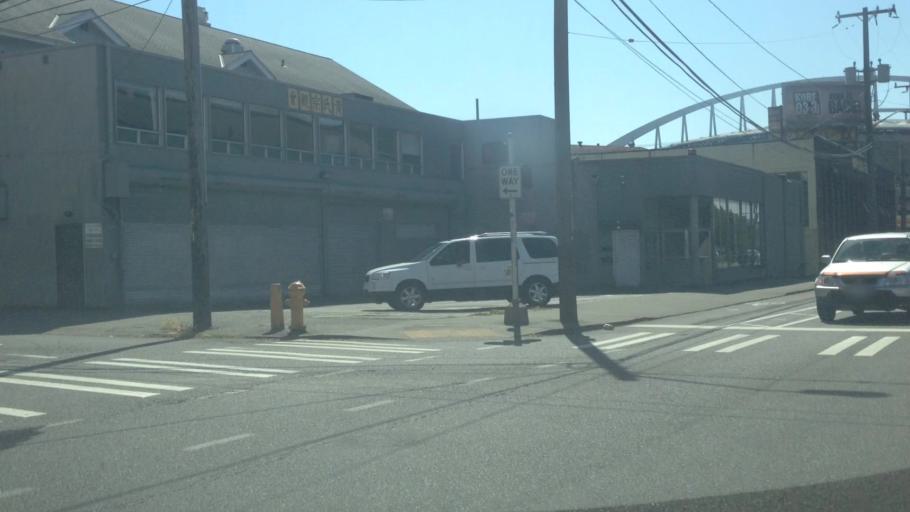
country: US
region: Washington
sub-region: King County
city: Seattle
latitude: 47.5958
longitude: -122.3250
